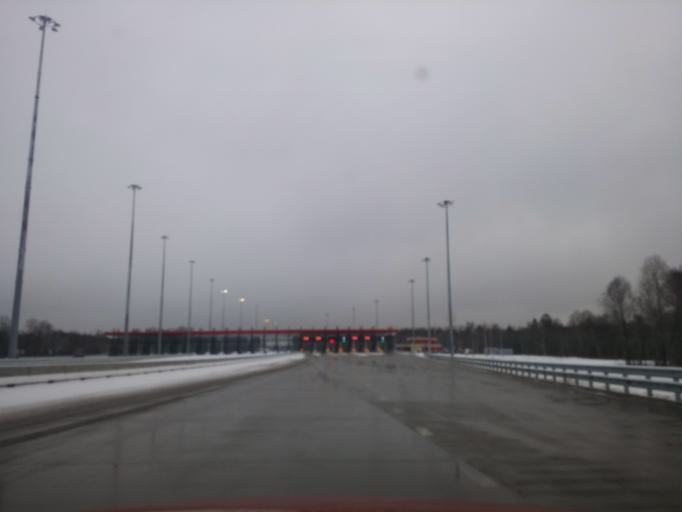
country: RU
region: Tverskaya
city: Likhoslavl'
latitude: 56.9571
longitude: 35.5033
